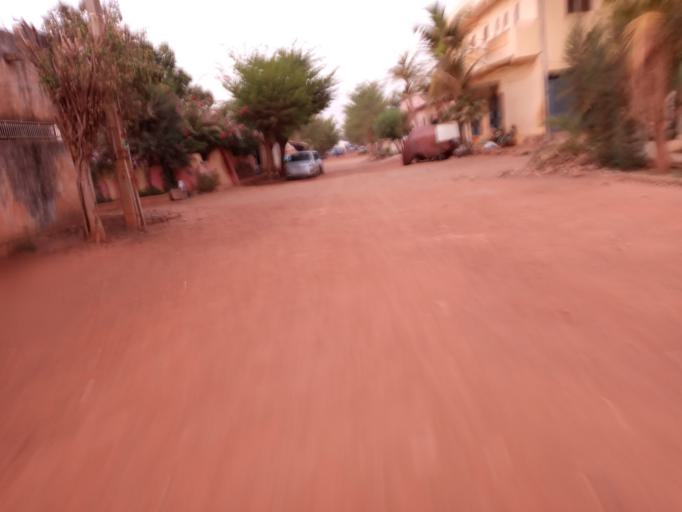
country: ML
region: Bamako
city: Bamako
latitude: 12.5810
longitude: -7.9534
